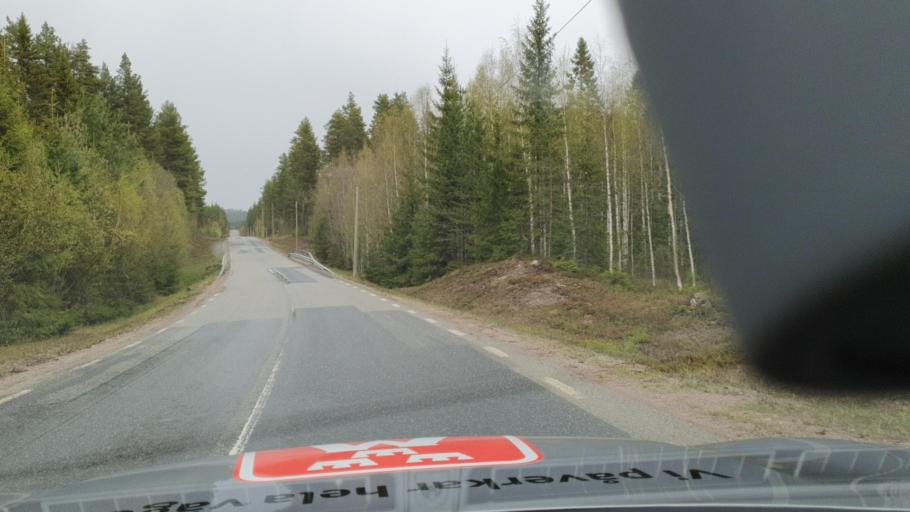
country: SE
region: Vaesternorrland
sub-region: Solleftea Kommun
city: As
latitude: 63.6944
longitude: 17.0308
